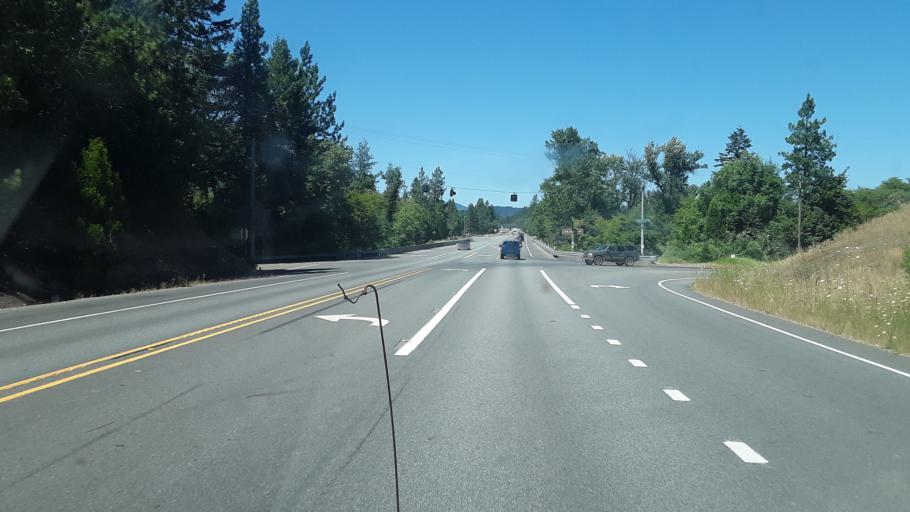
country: US
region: Oregon
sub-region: Josephine County
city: Cave Junction
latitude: 42.2700
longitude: -123.6194
